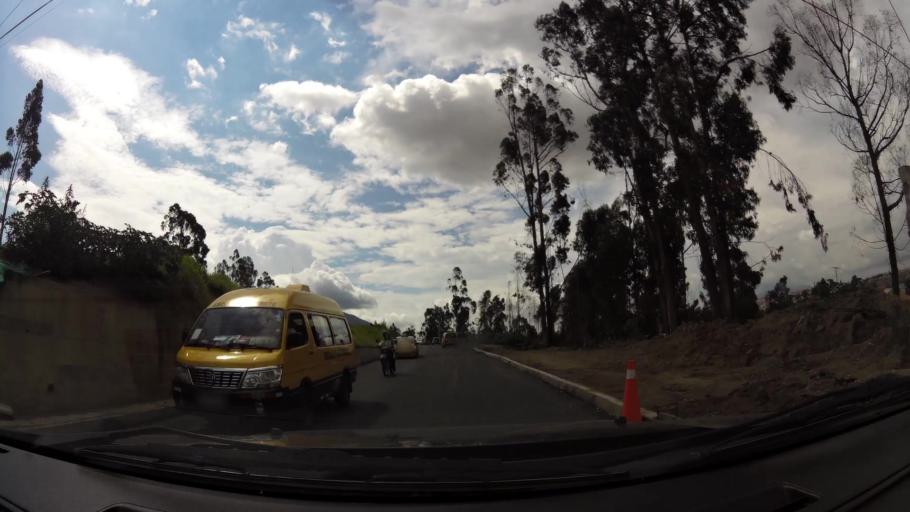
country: EC
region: Pichincha
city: Quito
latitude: -0.1033
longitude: -78.4595
